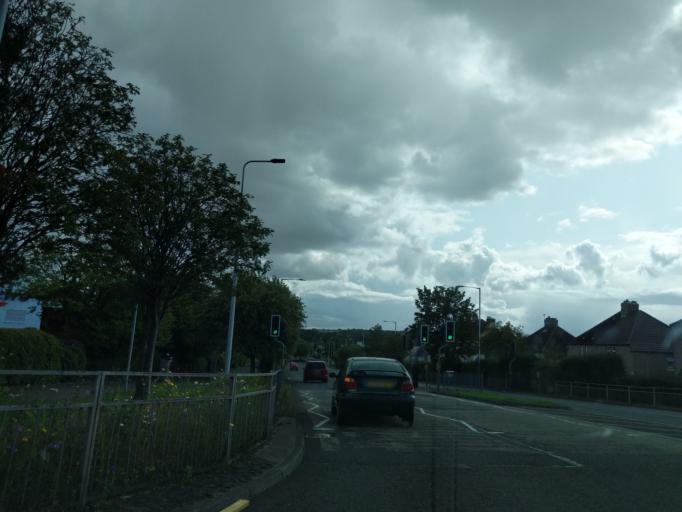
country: GB
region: Scotland
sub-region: Fife
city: Rosyth
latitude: 56.0444
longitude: -3.4273
